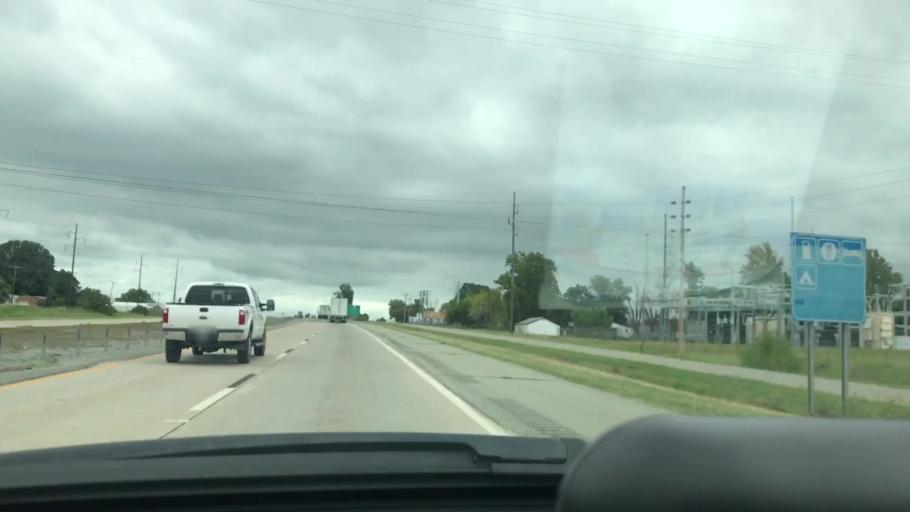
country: US
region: Oklahoma
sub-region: McIntosh County
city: Eufaula
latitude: 35.3547
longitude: -95.5759
